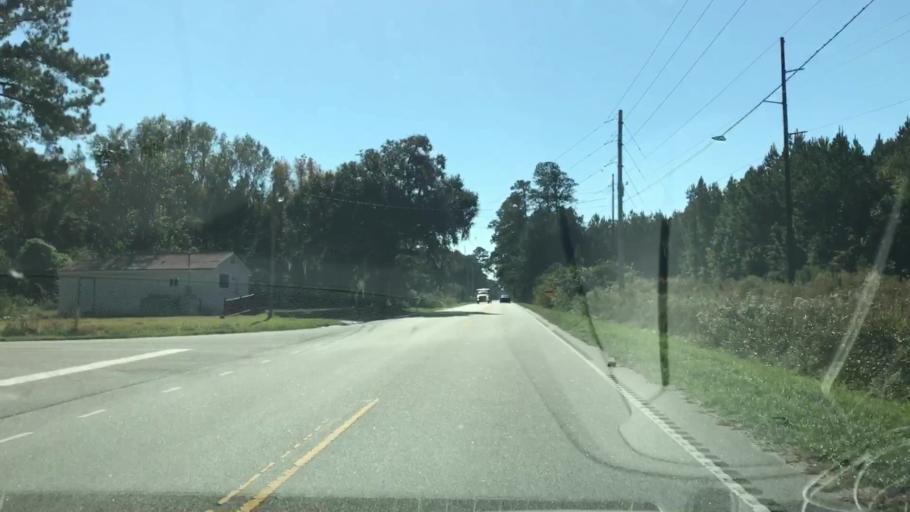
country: US
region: South Carolina
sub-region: Jasper County
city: Ridgeland
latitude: 32.5184
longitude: -80.8903
